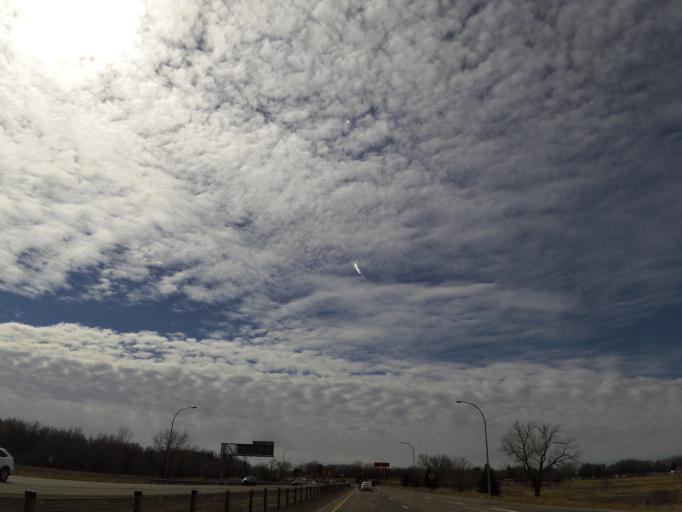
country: US
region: Minnesota
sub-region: Ramsey County
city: North Saint Paul
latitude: 45.0287
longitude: -92.9665
